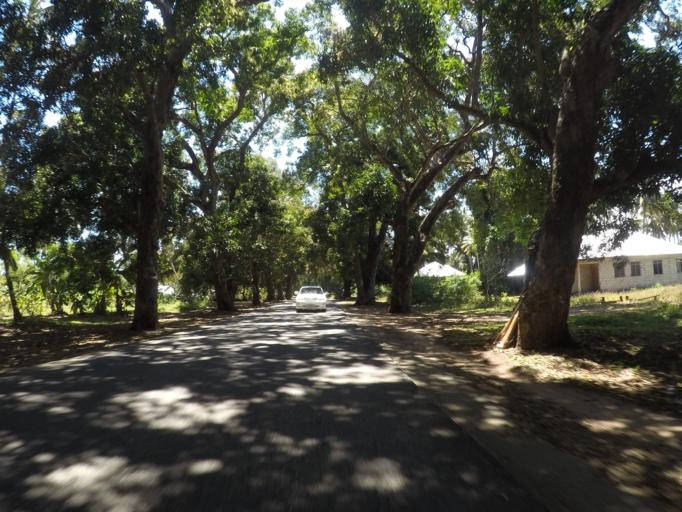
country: TZ
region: Zanzibar Central/South
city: Koani
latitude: -6.2664
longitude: 39.3428
